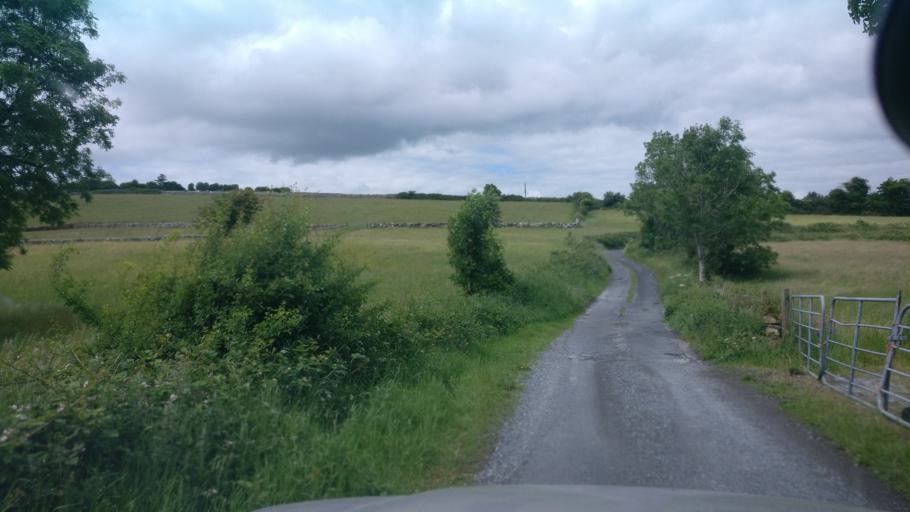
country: IE
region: Connaught
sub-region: County Galway
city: Loughrea
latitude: 53.1575
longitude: -8.5540
